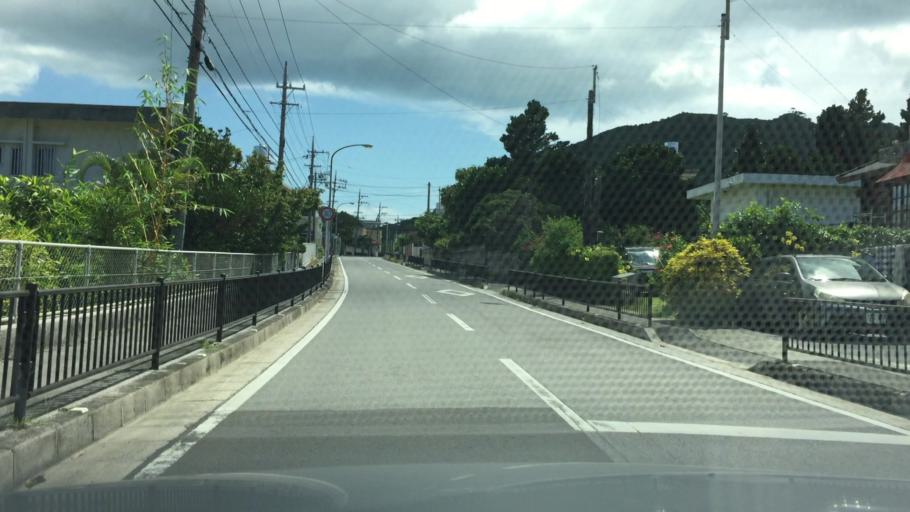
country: JP
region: Okinawa
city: Ishigaki
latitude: 24.4601
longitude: 124.1412
